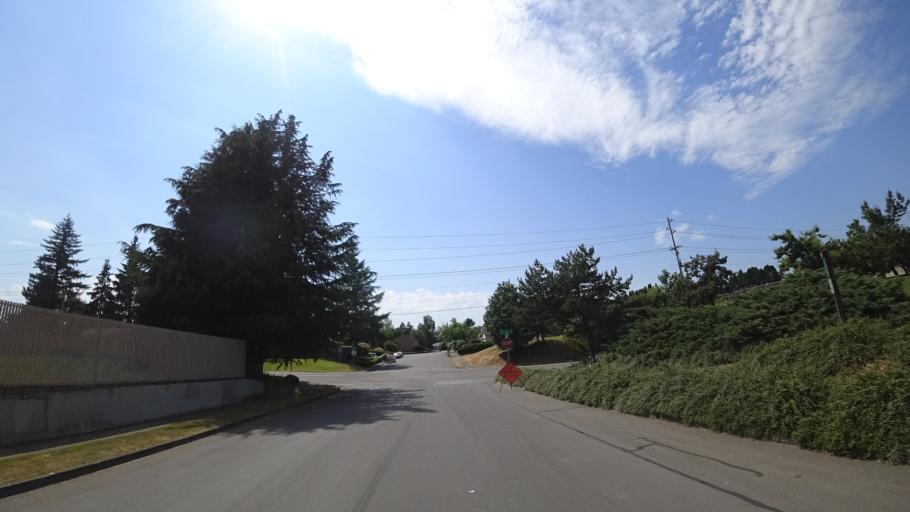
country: US
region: Oregon
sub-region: Multnomah County
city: Fairview
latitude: 45.5416
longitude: -122.4952
